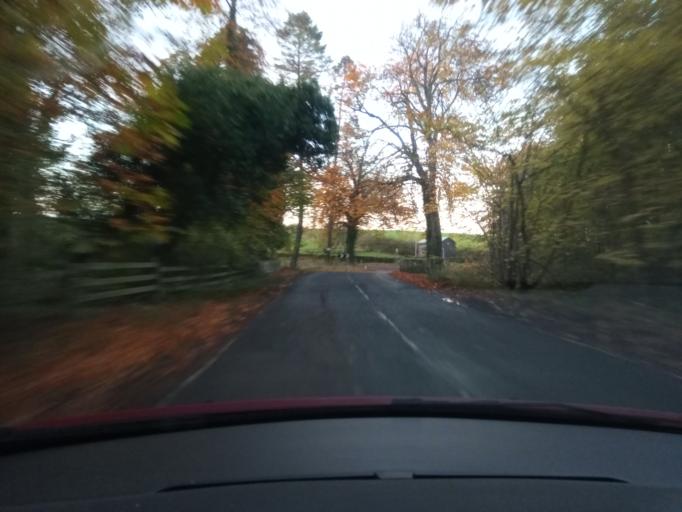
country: GB
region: England
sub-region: Northumberland
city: Bardon Mill
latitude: 54.9577
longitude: -2.2579
